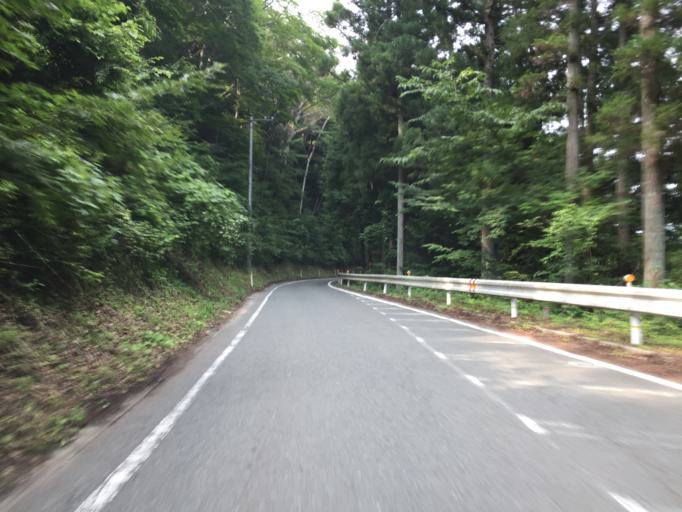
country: JP
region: Fukushima
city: Namie
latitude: 37.5703
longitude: 140.8776
